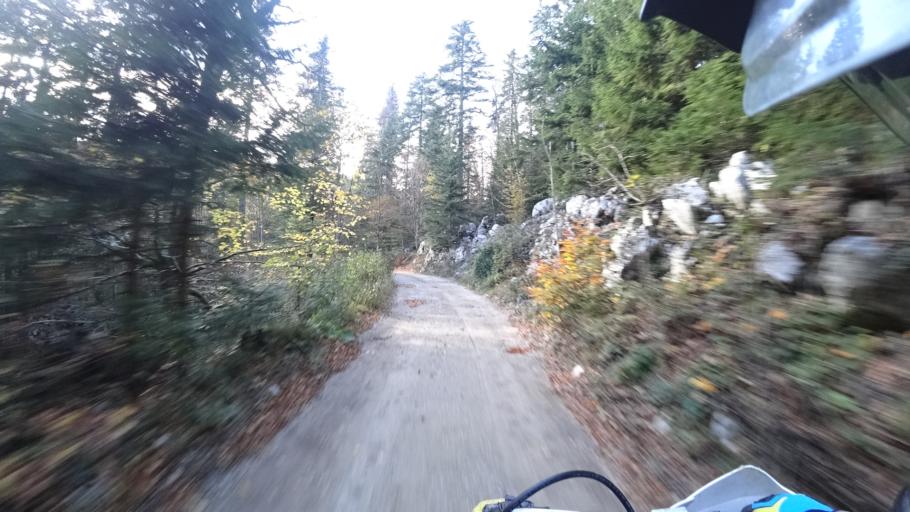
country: HR
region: Karlovacka
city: Plaski
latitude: 44.9370
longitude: 15.4515
